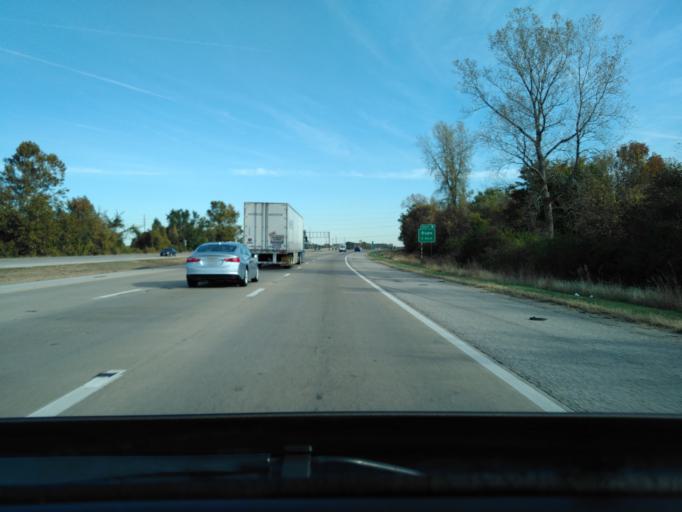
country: US
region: Illinois
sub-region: Saint Clair County
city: Dupo
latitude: 38.4905
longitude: -90.2177
